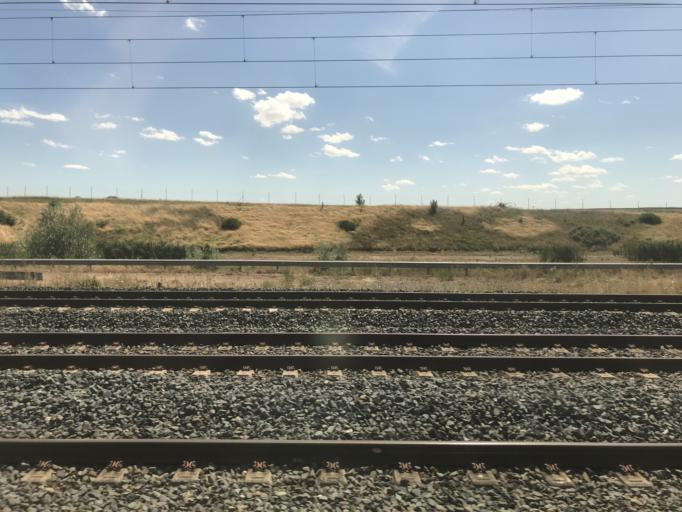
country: FR
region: Lorraine
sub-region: Departement de la Moselle
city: Verny
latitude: 48.9464
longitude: 6.1648
